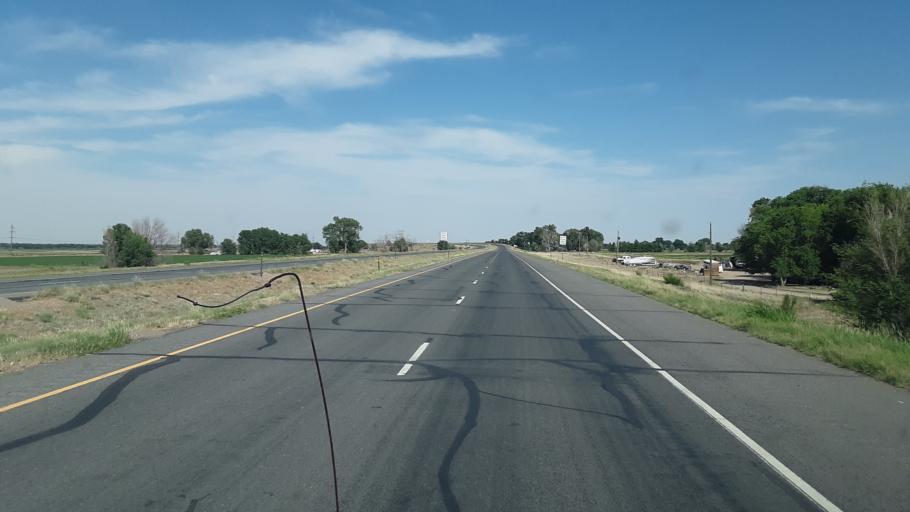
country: US
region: Colorado
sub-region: Otero County
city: Rocky Ford
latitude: 38.1039
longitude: -103.8546
